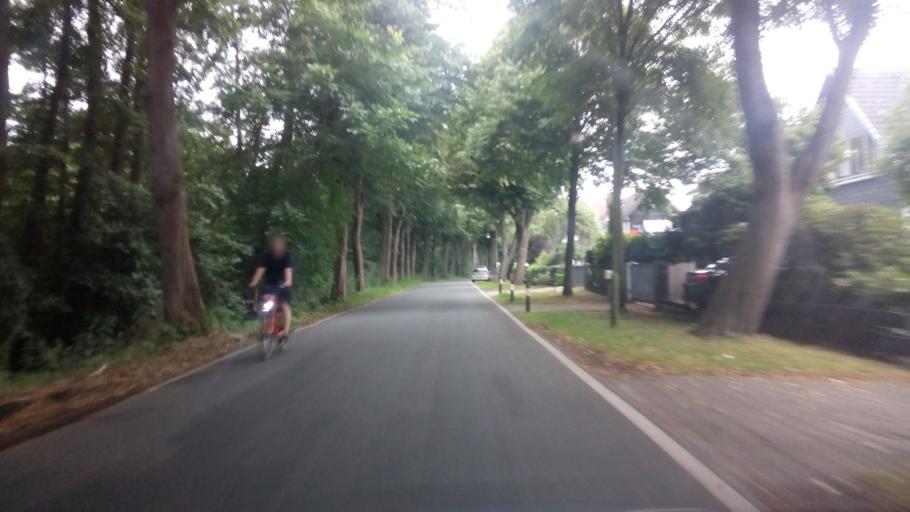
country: DE
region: Lower Saxony
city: Lilienthal
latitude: 53.1223
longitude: 8.8800
